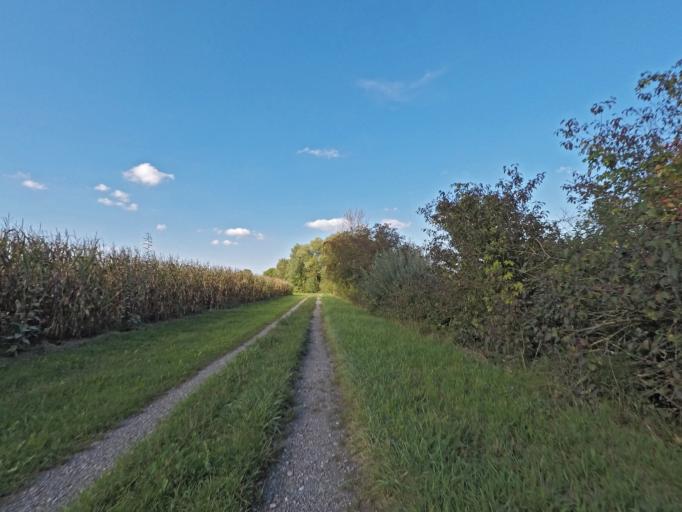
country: CH
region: Thurgau
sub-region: Frauenfeld District
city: Diessenhofen
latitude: 47.6609
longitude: 8.7470
